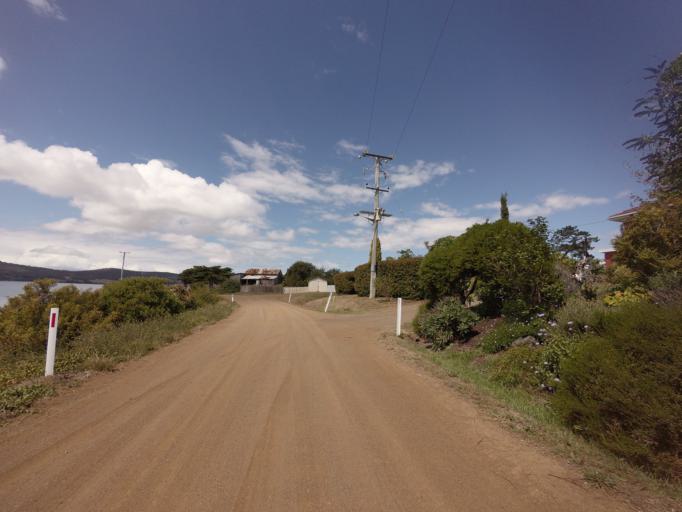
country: AU
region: Tasmania
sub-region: Clarence
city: Rokeby
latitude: -42.9160
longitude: 147.4338
